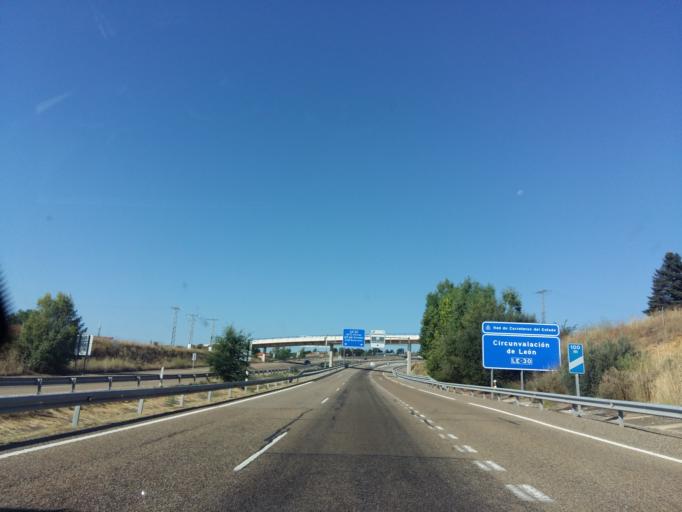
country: ES
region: Castille and Leon
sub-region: Provincia de Leon
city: Leon
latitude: 42.5682
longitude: -5.5868
